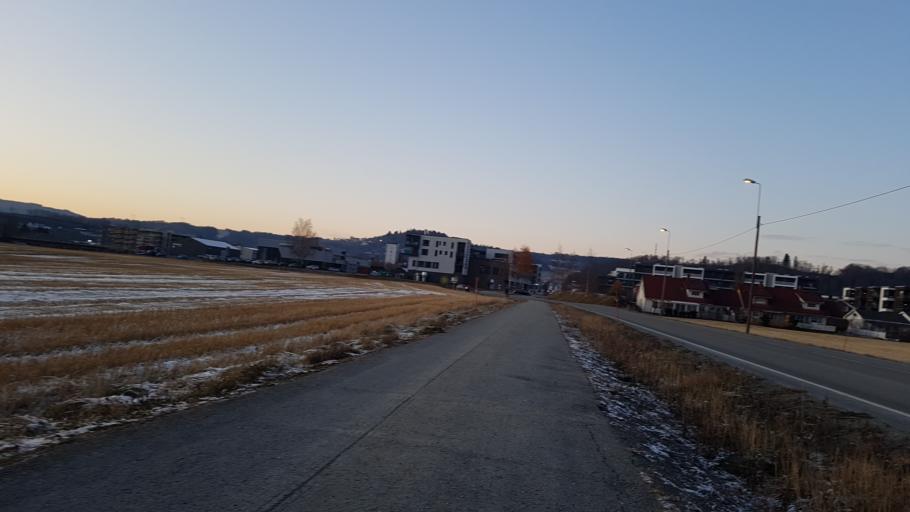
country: NO
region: Sor-Trondelag
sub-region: Melhus
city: Melhus
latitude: 63.2818
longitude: 10.2844
